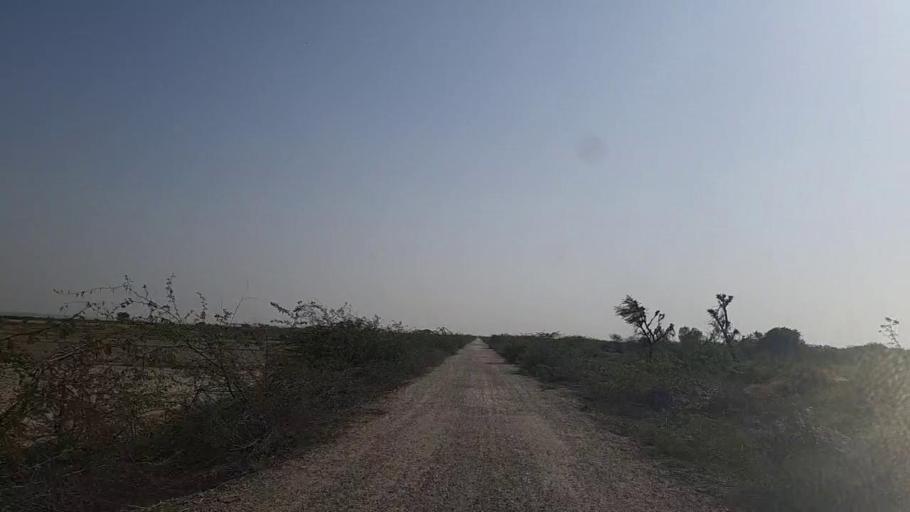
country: PK
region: Sindh
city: Naukot
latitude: 24.6026
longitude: 69.2650
